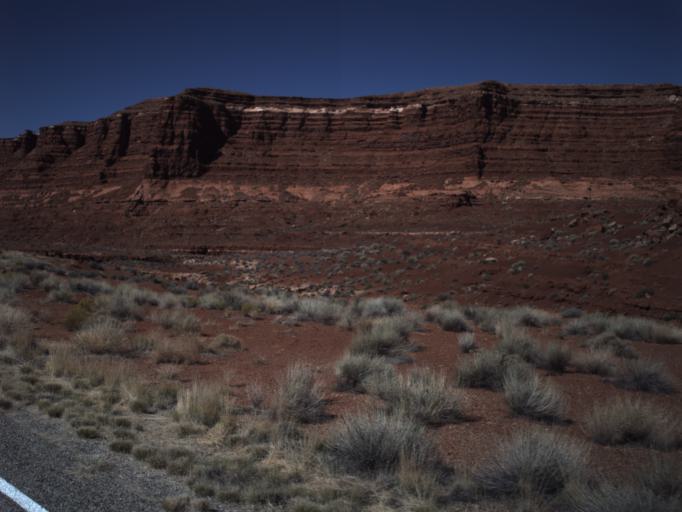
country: US
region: Utah
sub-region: San Juan County
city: Blanding
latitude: 37.8613
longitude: -110.3501
